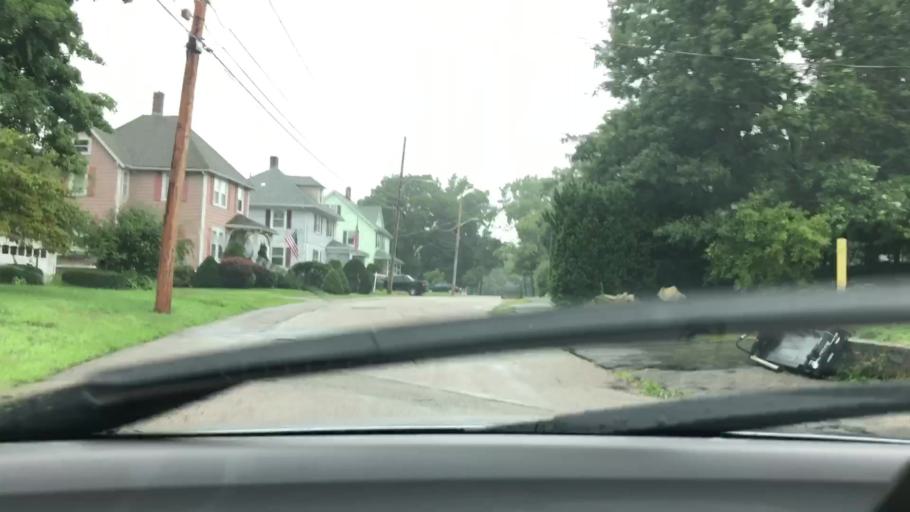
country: US
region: Massachusetts
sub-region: Norfolk County
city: Norwood
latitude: 42.1986
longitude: -71.2006
